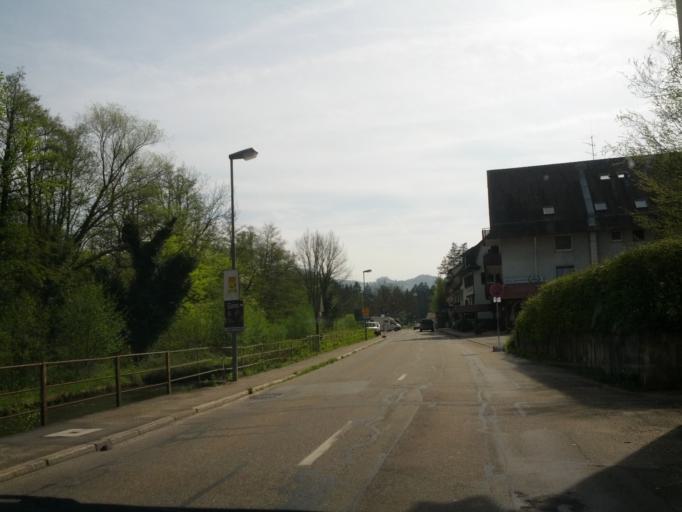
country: DE
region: Baden-Wuerttemberg
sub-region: Freiburg Region
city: Gutach im Breisgau
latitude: 48.1160
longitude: 7.9858
